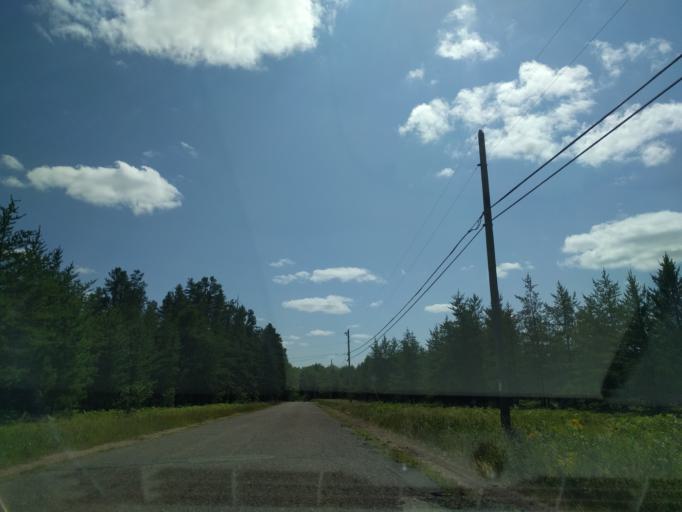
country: US
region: Michigan
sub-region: Marquette County
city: K. I. Sawyer Air Force Base
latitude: 46.2818
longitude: -87.3663
